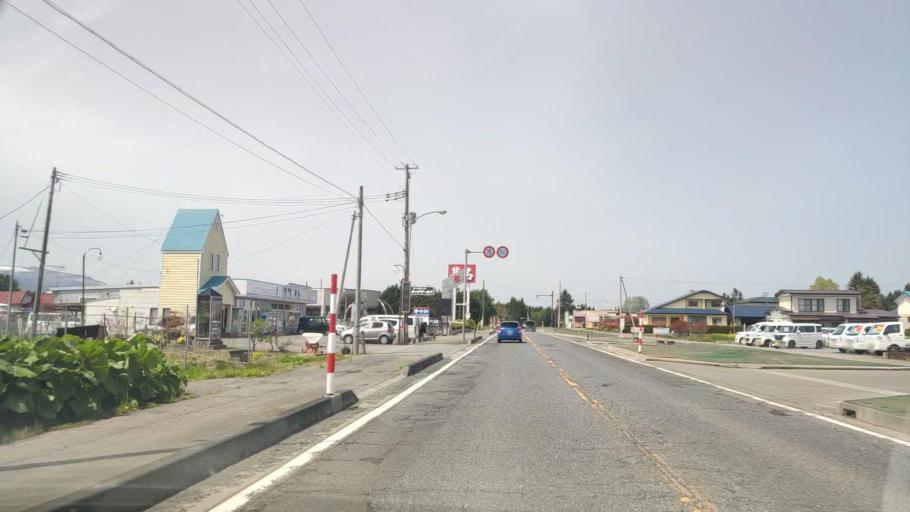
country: JP
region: Aomori
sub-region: Misawa Shi
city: Inuotose
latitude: 40.6754
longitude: 141.1761
